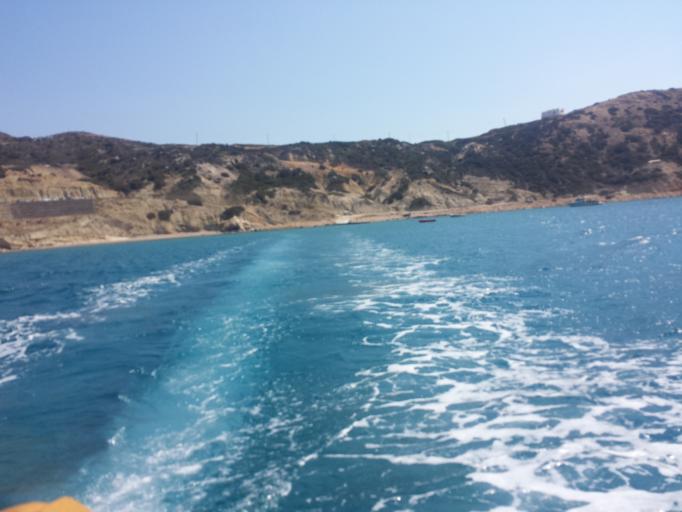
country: GR
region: South Aegean
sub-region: Nomos Kykladon
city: Adamas
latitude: 36.6610
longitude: 24.4275
